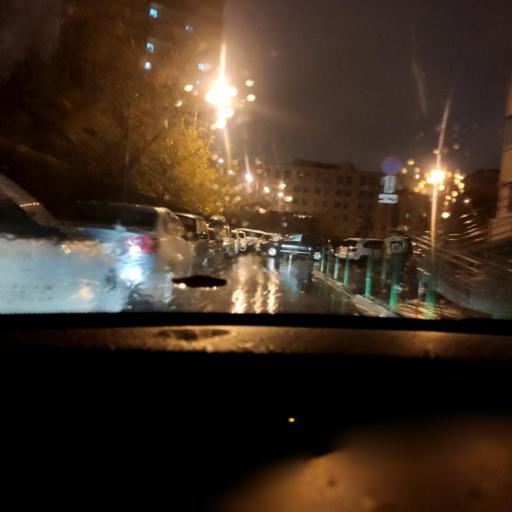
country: RU
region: Samara
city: Samara
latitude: 53.2163
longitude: 50.1715
